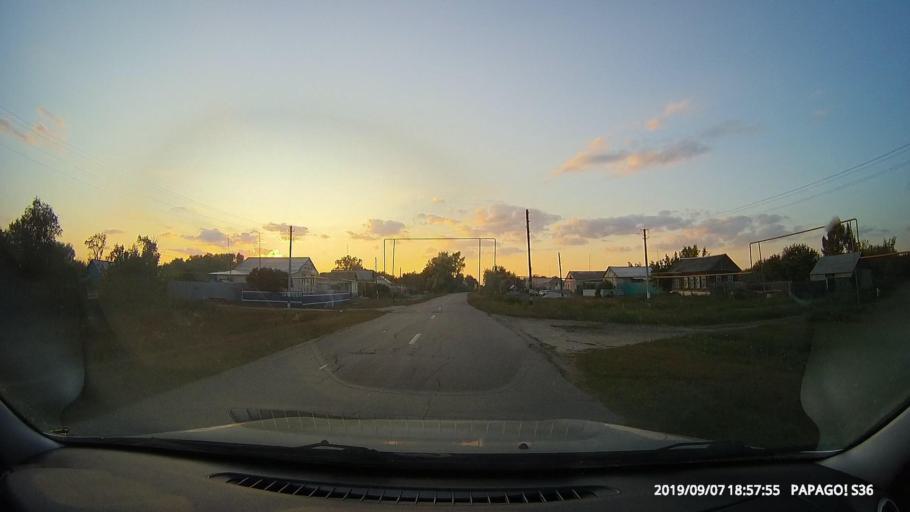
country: RU
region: Samara
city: Chapayevsk
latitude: 52.9946
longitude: 49.7764
